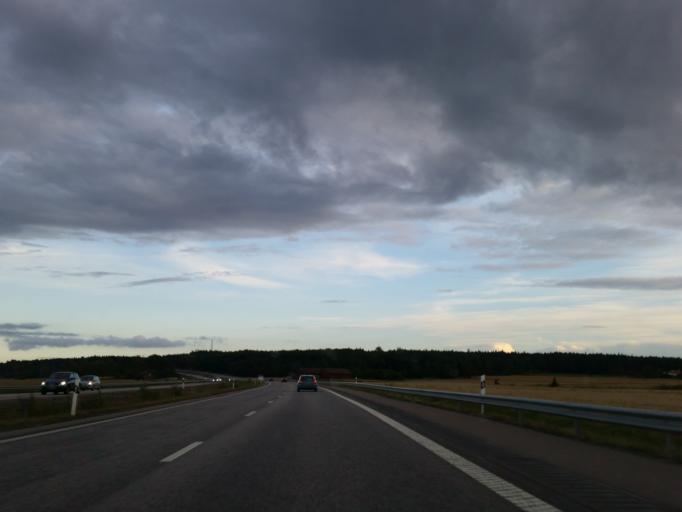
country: SE
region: Uppsala
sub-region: Uppsala Kommun
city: Saevja
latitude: 59.8116
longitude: 17.7563
